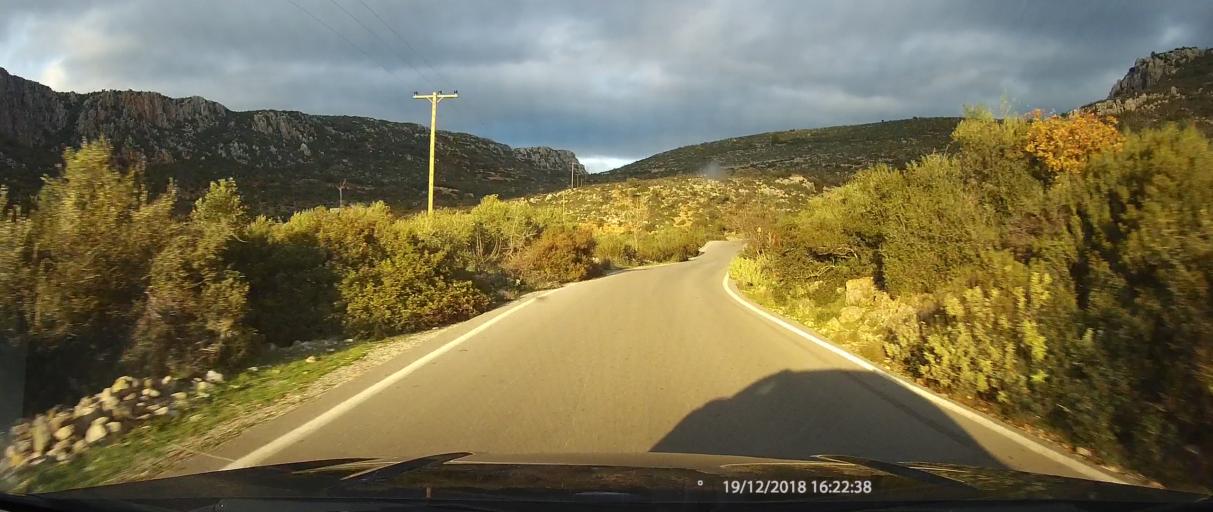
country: GR
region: Peloponnese
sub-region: Nomos Lakonias
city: Kato Glikovrisi
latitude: 36.9442
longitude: 22.8307
